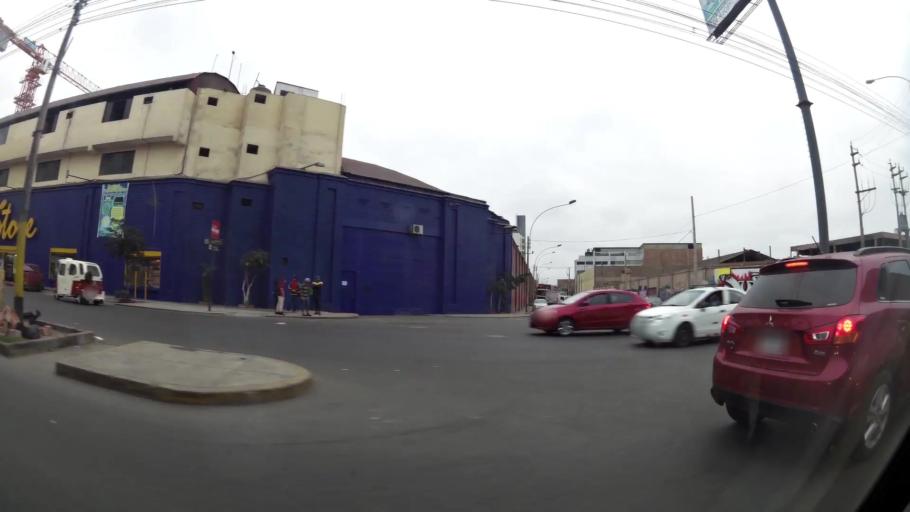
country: PE
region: Lima
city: Lima
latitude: -12.0492
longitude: -77.0526
